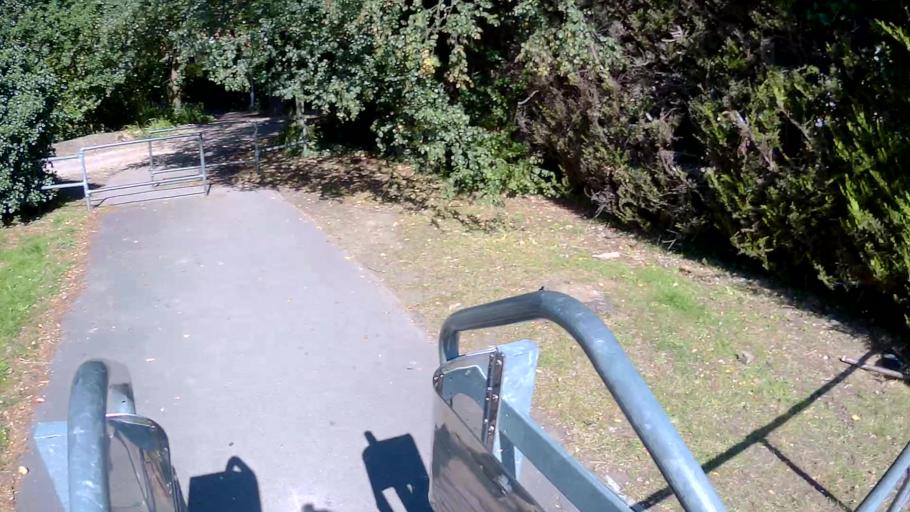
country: GB
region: England
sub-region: Bracknell Forest
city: Crowthorne
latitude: 51.3784
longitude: -0.8013
